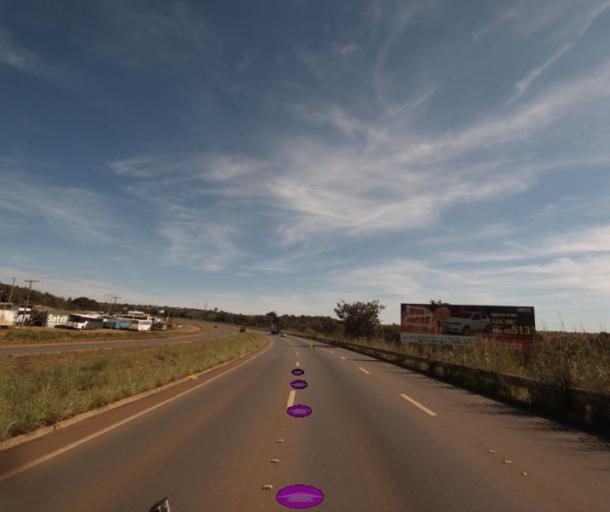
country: BR
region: Federal District
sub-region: Brasilia
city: Brasilia
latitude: -15.7658
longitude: -48.2304
